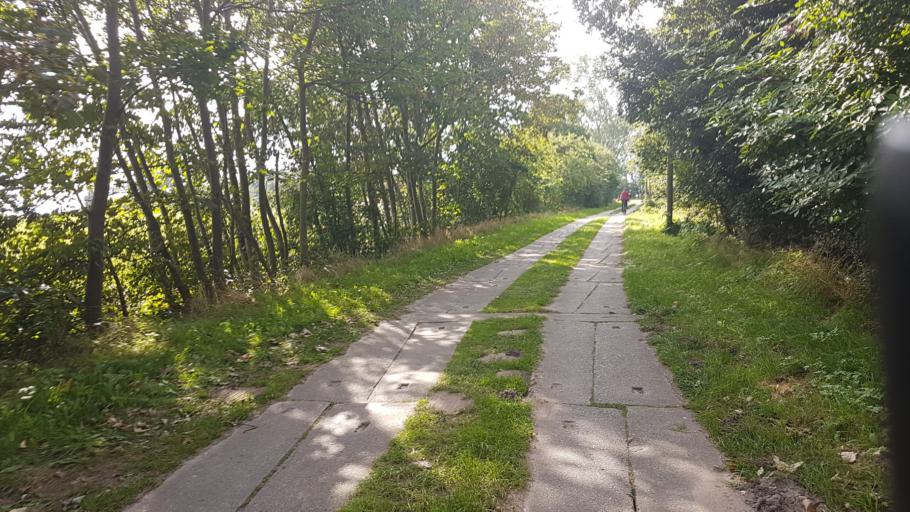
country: DE
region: Mecklenburg-Vorpommern
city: Rambin
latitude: 54.4473
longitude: 13.1330
